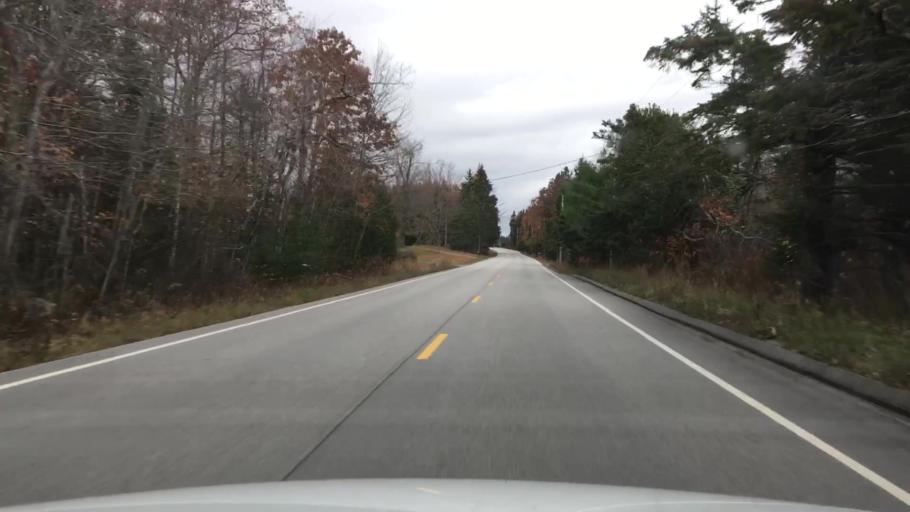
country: US
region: Maine
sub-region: Hancock County
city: Penobscot
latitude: 44.4739
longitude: -68.6372
